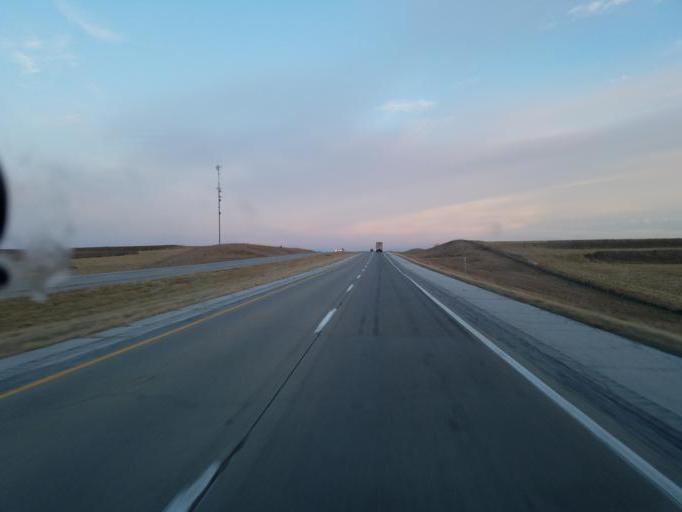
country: US
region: Iowa
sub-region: Pottawattamie County
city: Avoca
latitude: 41.4990
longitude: -95.4703
